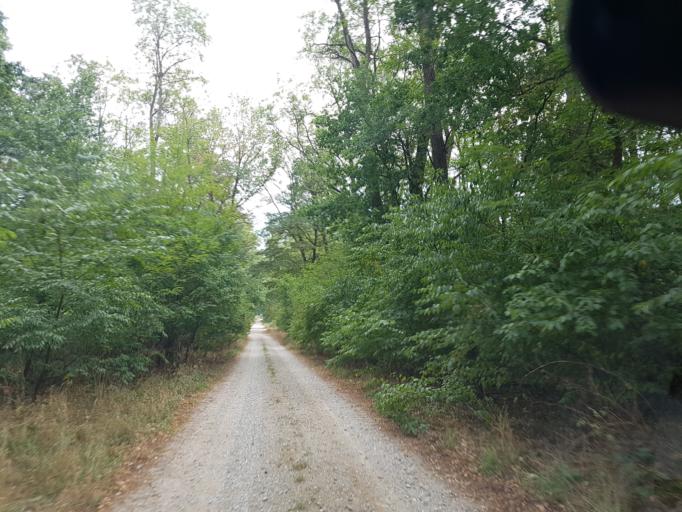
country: DE
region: Saxony-Anhalt
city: Rosslau
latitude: 52.0267
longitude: 12.2882
